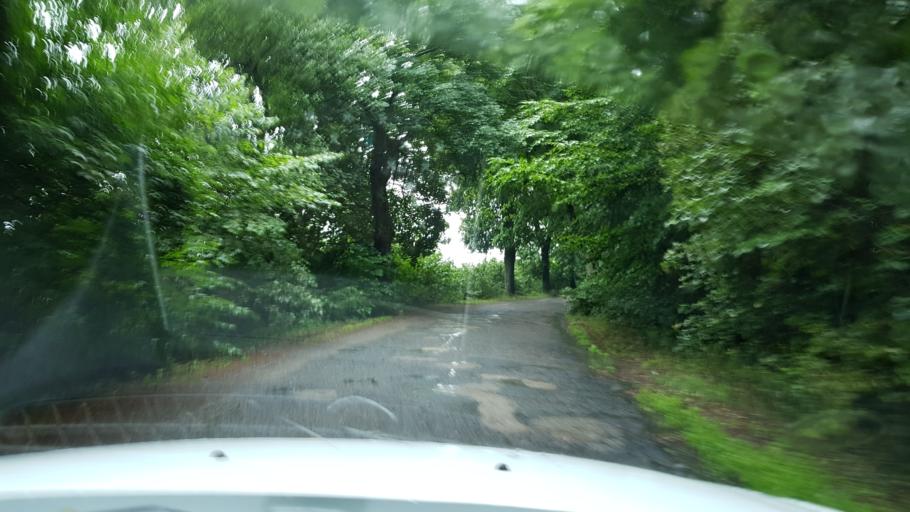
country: PL
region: West Pomeranian Voivodeship
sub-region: Powiat gryficki
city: Brojce
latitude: 53.9537
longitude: 15.4391
